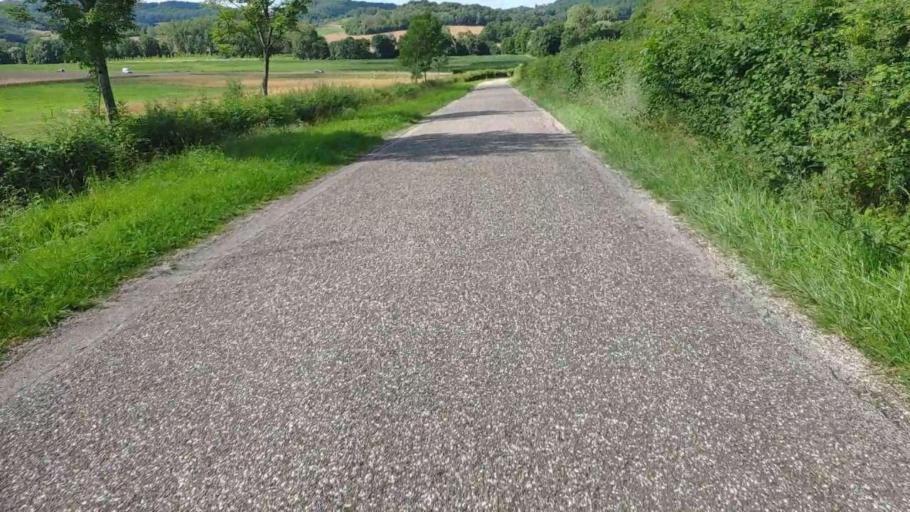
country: FR
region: Franche-Comte
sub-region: Departement du Jura
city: Poligny
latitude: 46.8202
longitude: 5.5829
